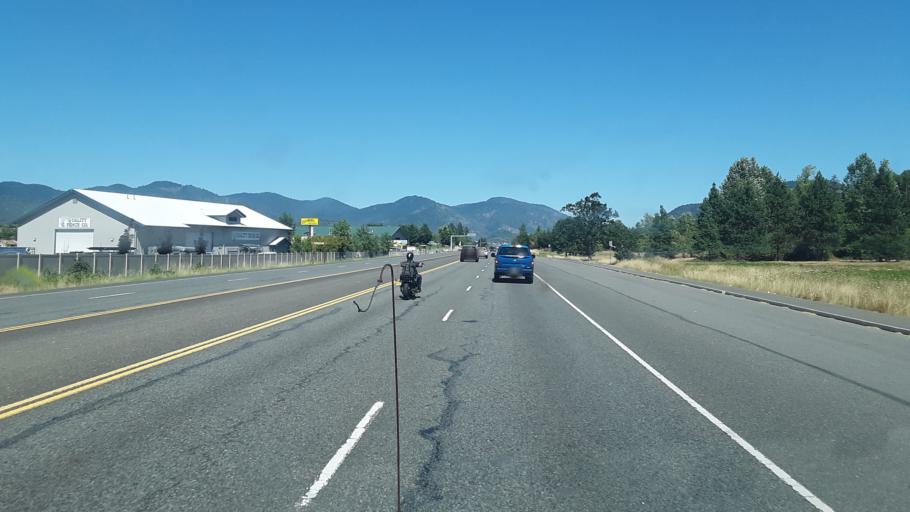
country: US
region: Oregon
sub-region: Josephine County
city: Redwood
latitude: 42.4196
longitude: -123.3610
